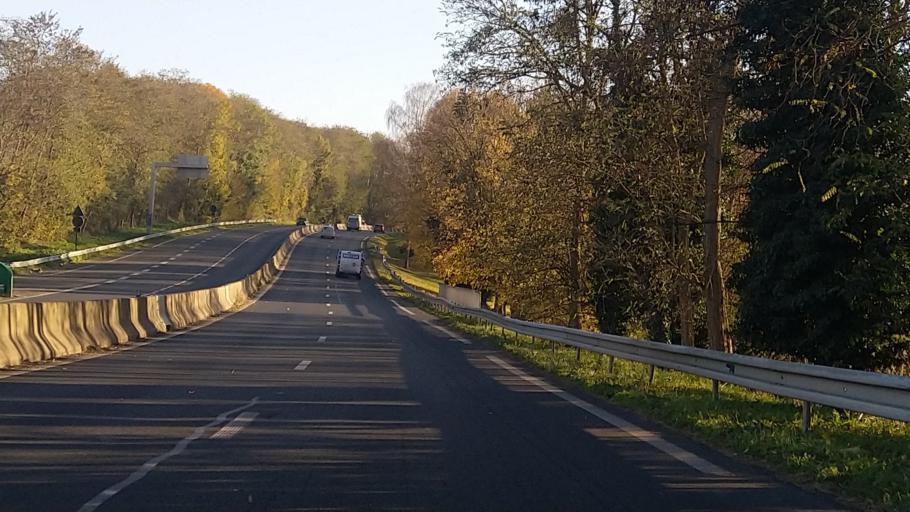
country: FR
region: Ile-de-France
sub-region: Departement du Val-d'Oise
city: Saint-Brice-sous-Foret
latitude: 49.0065
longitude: 2.3548
